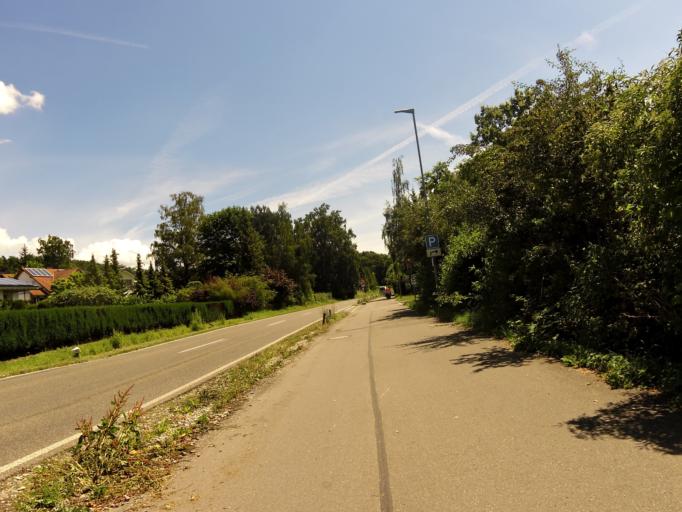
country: DE
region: Baden-Wuerttemberg
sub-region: Tuebingen Region
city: Uhldingen-Muhlhofen
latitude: 47.7161
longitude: 9.2354
